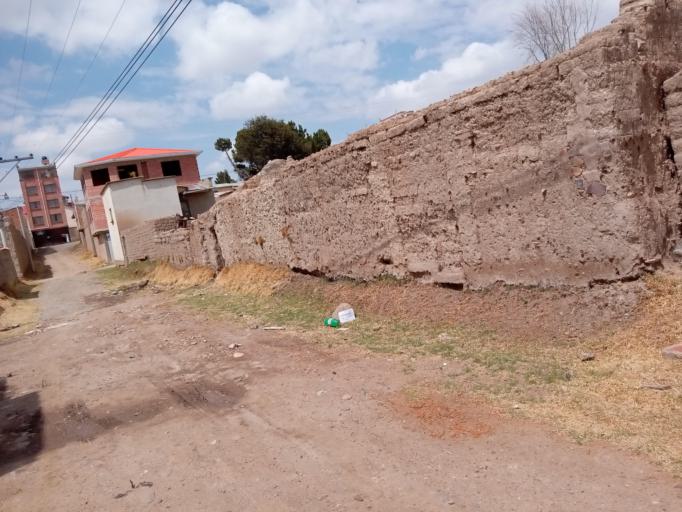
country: BO
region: La Paz
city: Batallas
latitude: -16.3991
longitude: -68.4791
